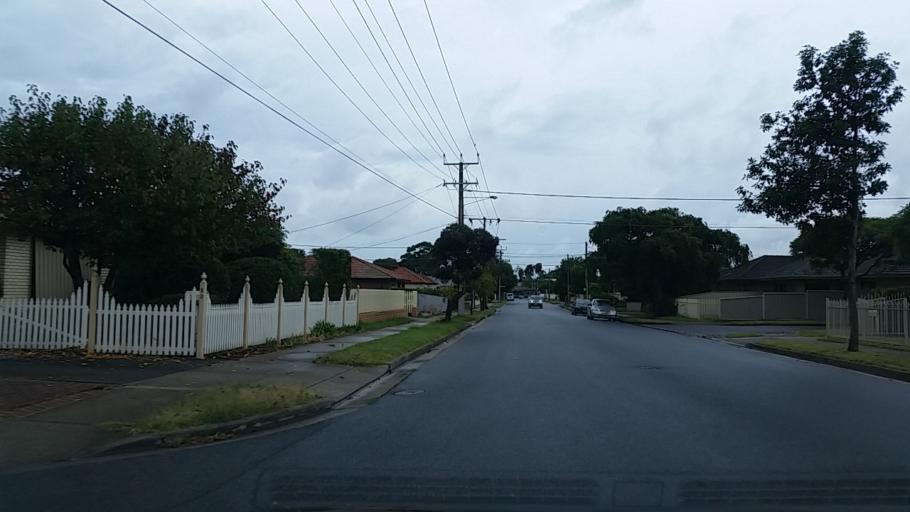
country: AU
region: South Australia
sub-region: Charles Sturt
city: Seaton
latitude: -34.8986
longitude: 138.5201
